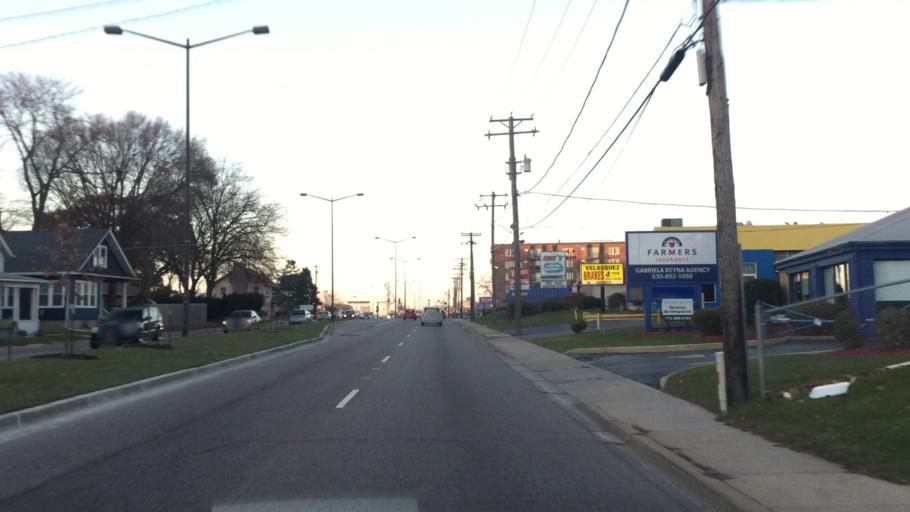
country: US
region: Illinois
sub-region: Kane County
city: Aurora
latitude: 41.7717
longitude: -88.3138
